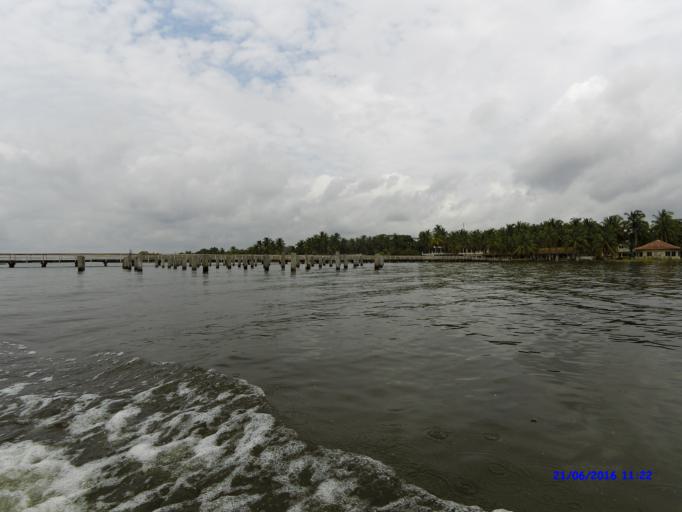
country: BJ
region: Mono
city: Come
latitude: 6.5289
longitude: 1.9715
